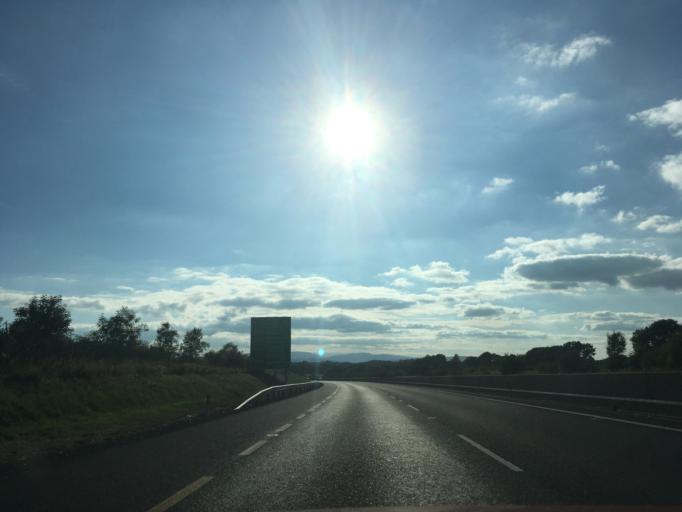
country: IE
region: Munster
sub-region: Waterford
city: Waterford
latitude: 52.2901
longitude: -7.1101
